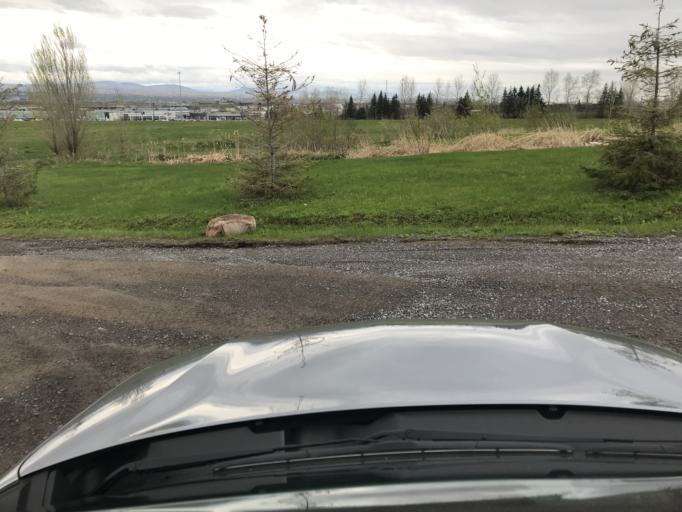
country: CA
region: Quebec
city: L'Ancienne-Lorette
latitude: 46.7917
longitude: -71.2824
